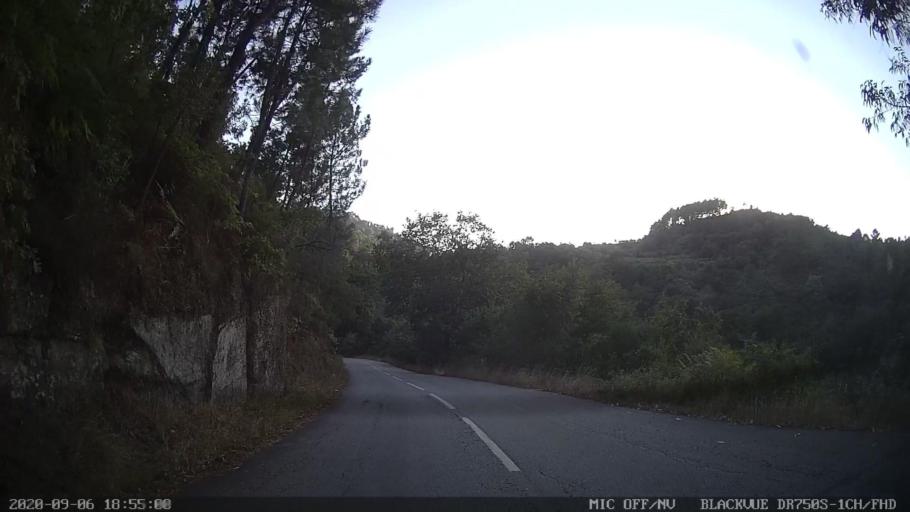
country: PT
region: Porto
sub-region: Baiao
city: Baiao
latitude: 41.2471
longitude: -7.9874
